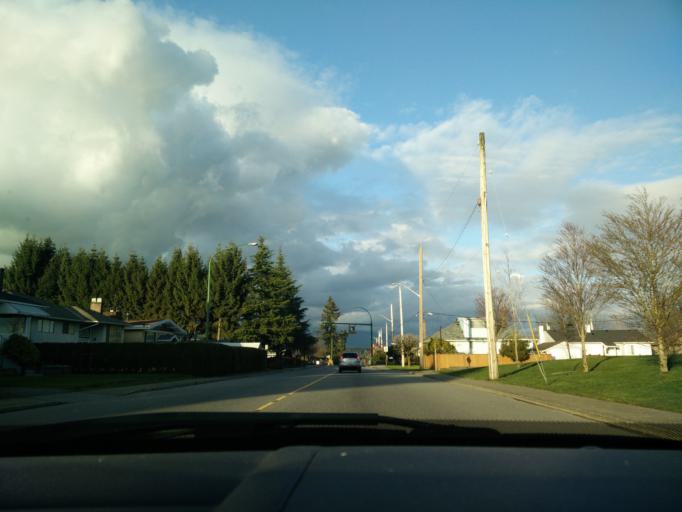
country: CA
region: British Columbia
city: New Westminster
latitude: 49.2301
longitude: -122.9072
